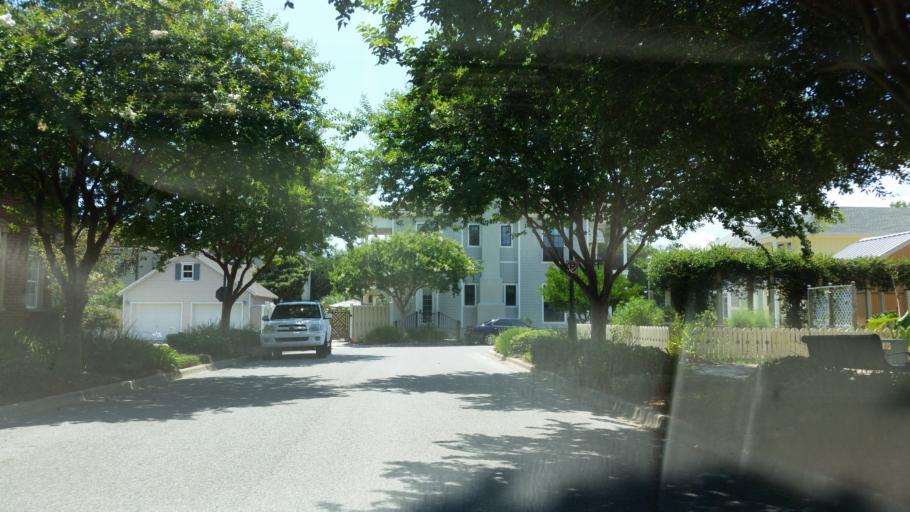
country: US
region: Florida
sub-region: Escambia County
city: Pensacola
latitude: 30.4138
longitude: -87.2075
